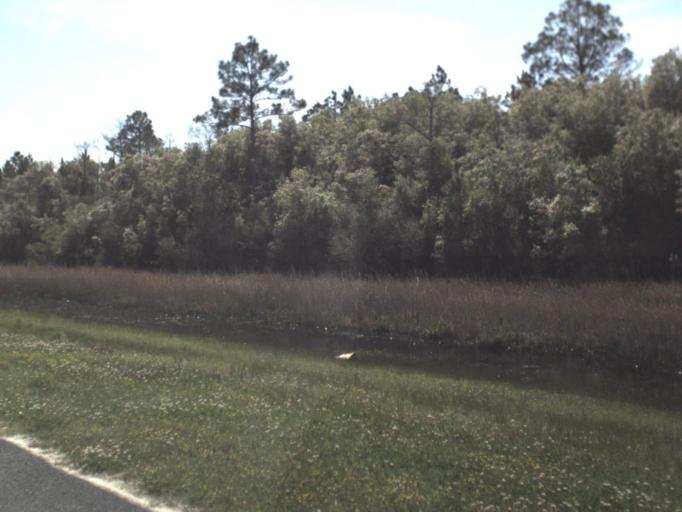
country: US
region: Florida
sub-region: Bay County
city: Lynn Haven
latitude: 30.3358
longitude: -85.6601
